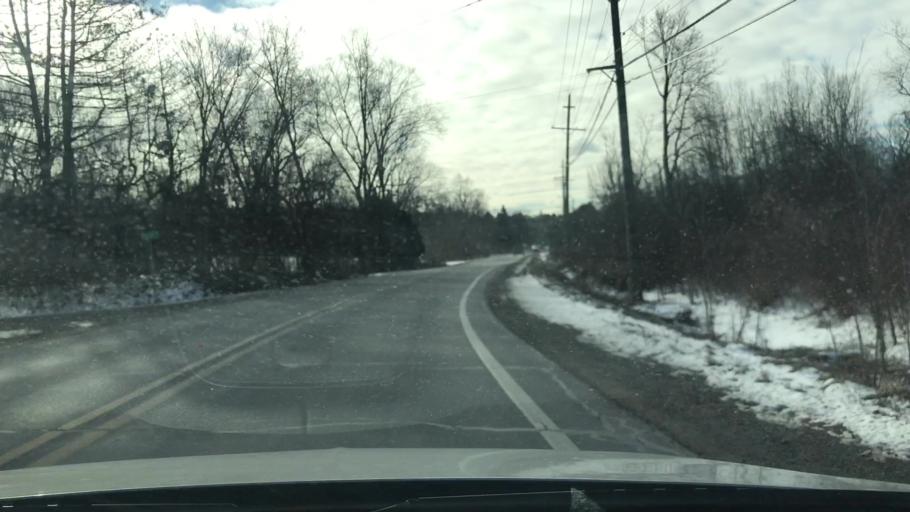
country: US
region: Michigan
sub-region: Oakland County
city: Rochester
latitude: 42.7275
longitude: -83.1566
